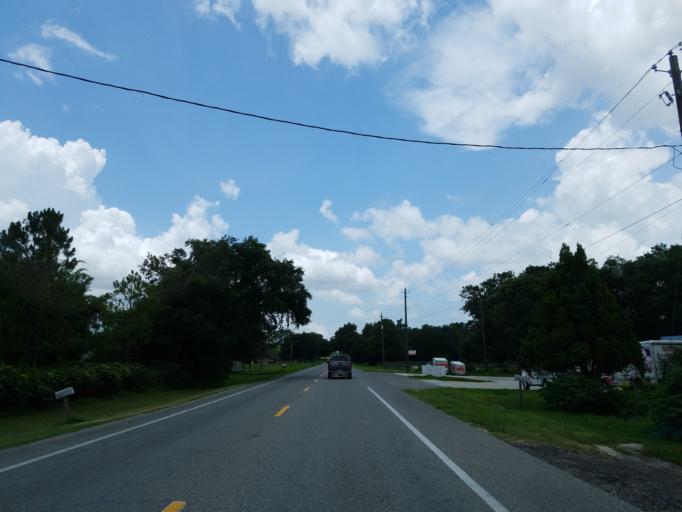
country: US
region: Florida
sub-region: Polk County
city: Willow Oak
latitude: 27.8506
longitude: -82.0776
